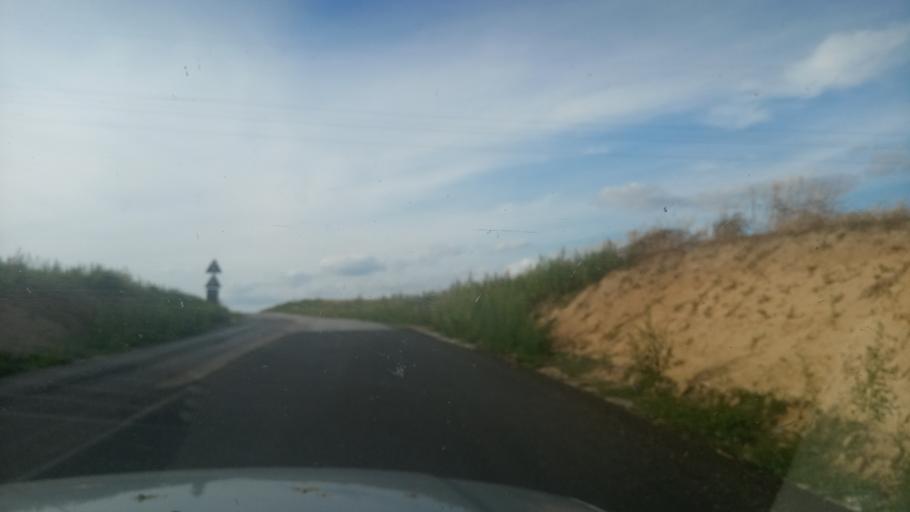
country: PL
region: Kujawsko-Pomorskie
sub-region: Powiat nakielski
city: Sadki
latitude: 53.1972
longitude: 17.3852
